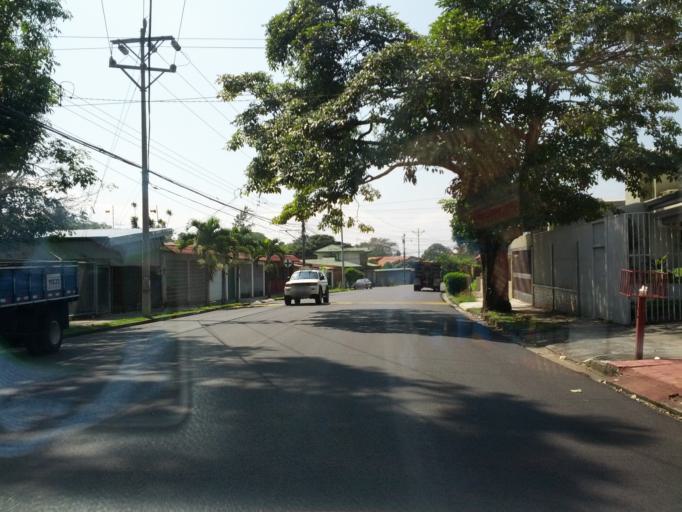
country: CR
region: Alajuela
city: Alajuela
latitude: 10.0126
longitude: -84.2035
